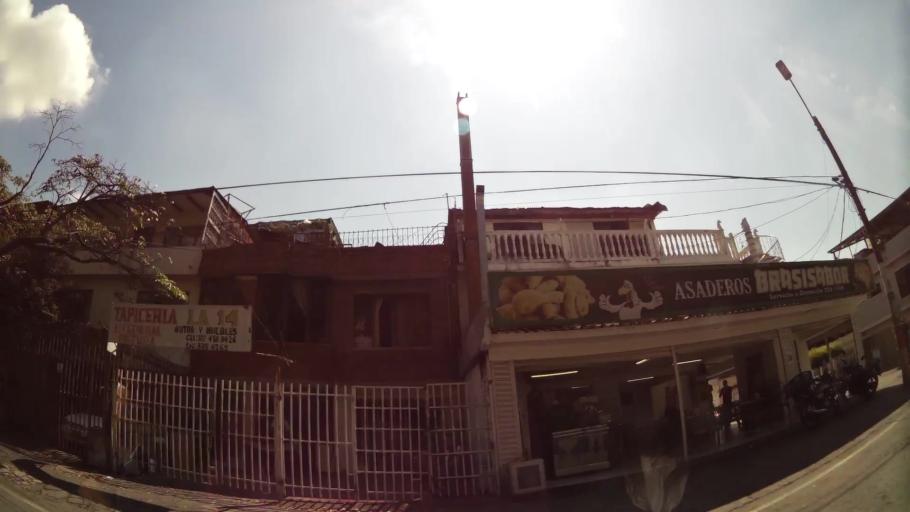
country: CO
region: Valle del Cauca
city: Cali
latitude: 3.4217
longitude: -76.5274
